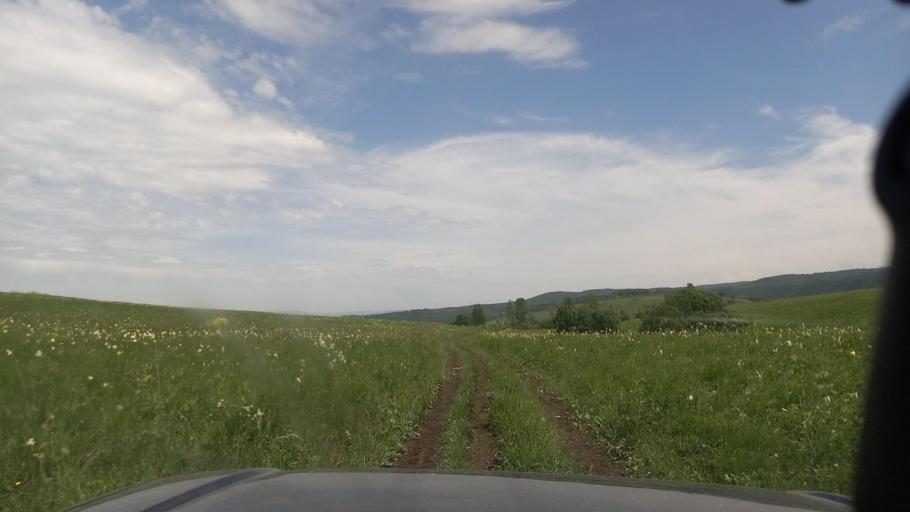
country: RU
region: Karachayevo-Cherkesiya
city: Pregradnaya
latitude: 44.0673
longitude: 41.3032
